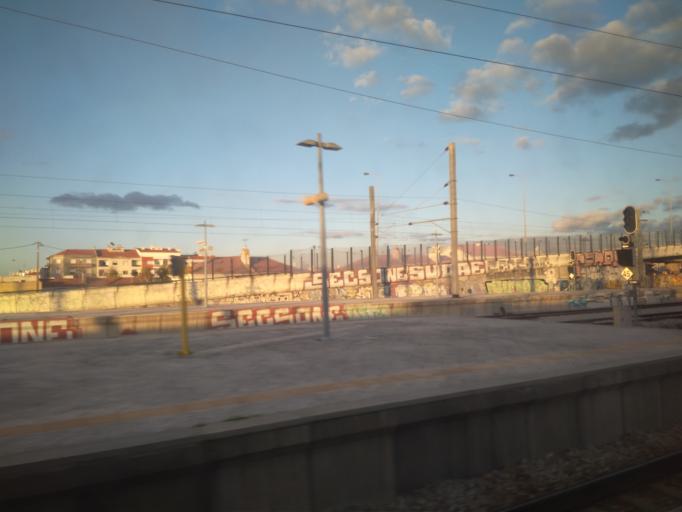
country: PT
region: Setubal
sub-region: Palmela
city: Pinhal Novo
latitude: 38.6300
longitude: -8.9109
